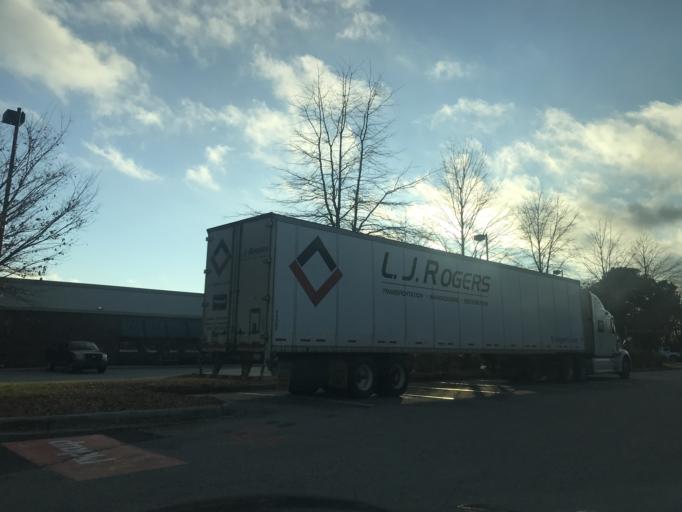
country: US
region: North Carolina
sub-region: Wake County
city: Wake Forest
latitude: 35.9501
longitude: -78.5340
